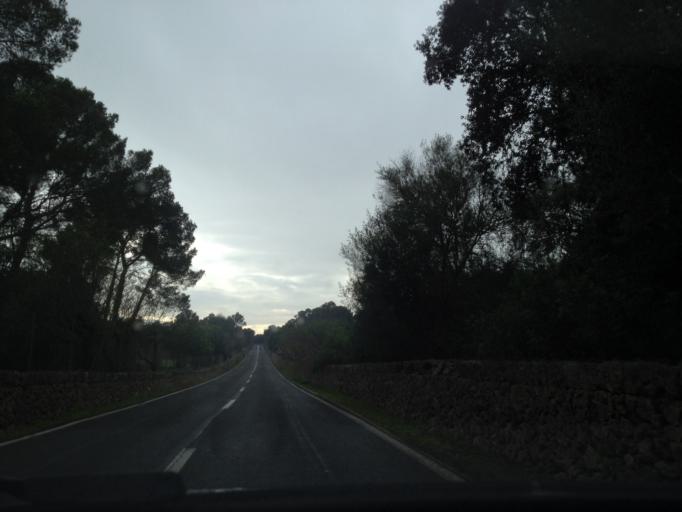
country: ES
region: Balearic Islands
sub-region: Illes Balears
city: Sineu
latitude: 39.6602
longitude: 3.0103
